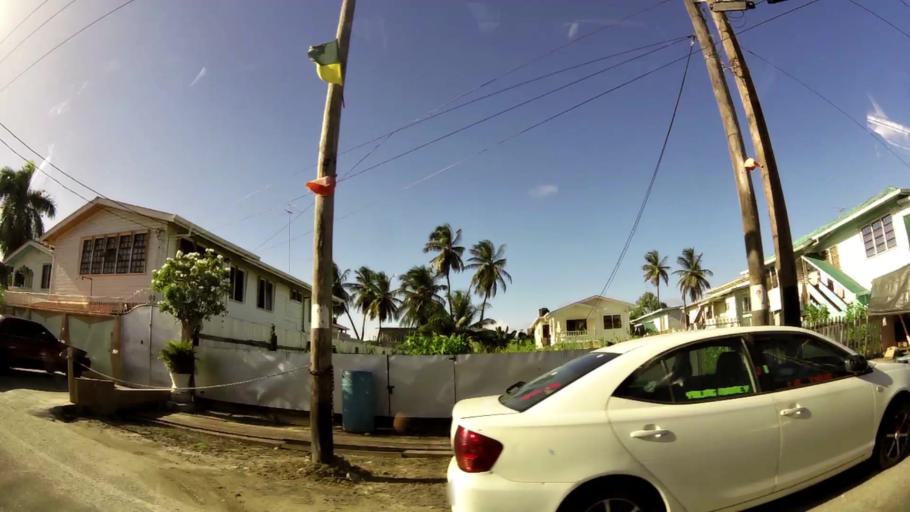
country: GY
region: Demerara-Mahaica
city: Georgetown
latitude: 6.8177
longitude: -58.1431
